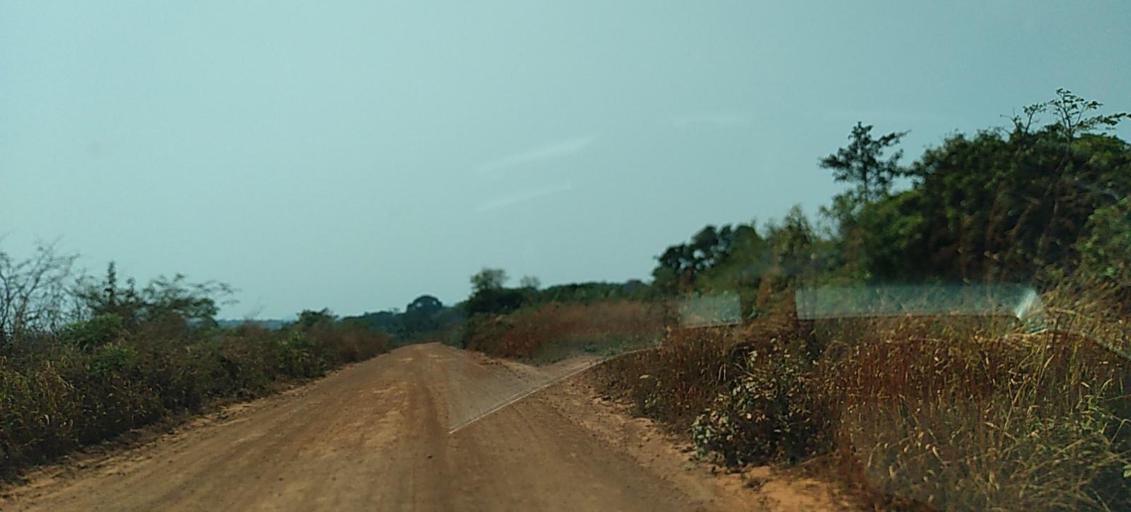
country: ZM
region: North-Western
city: Kansanshi
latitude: -12.0076
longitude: 26.5511
